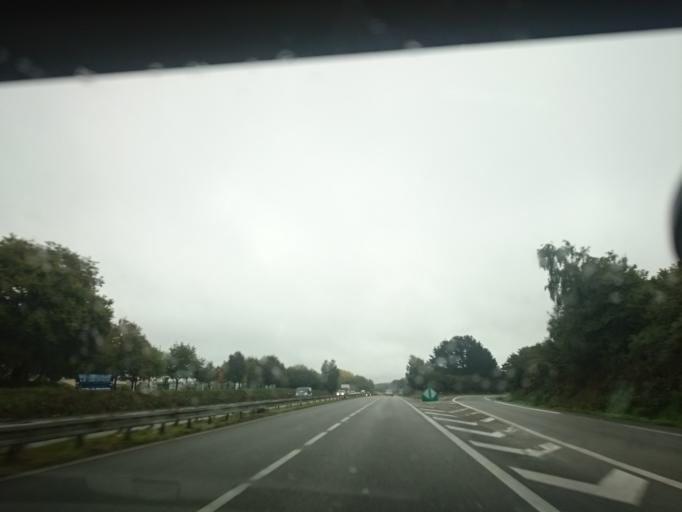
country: FR
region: Brittany
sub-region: Departement du Morbihan
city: Hennebont
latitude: 47.7885
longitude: -3.2517
